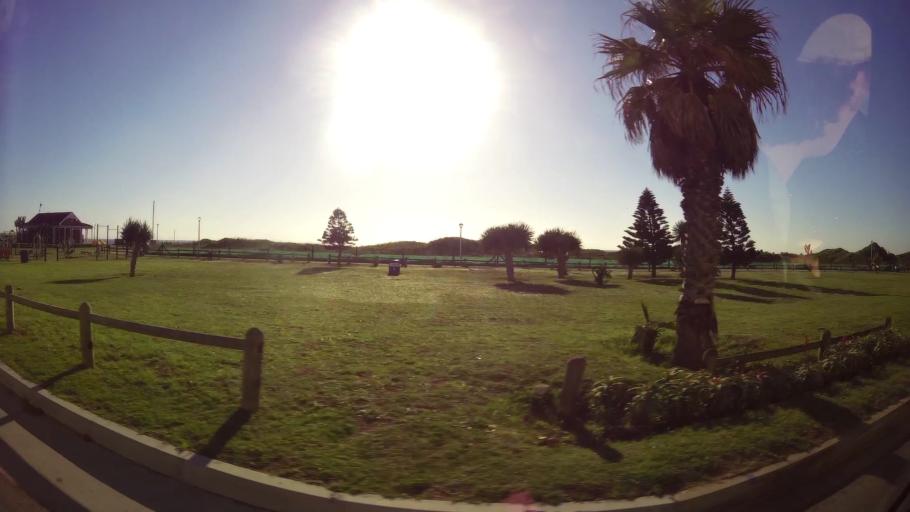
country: ZA
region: Eastern Cape
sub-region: Nelson Mandela Bay Metropolitan Municipality
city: Port Elizabeth
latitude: -33.9888
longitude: 25.6728
